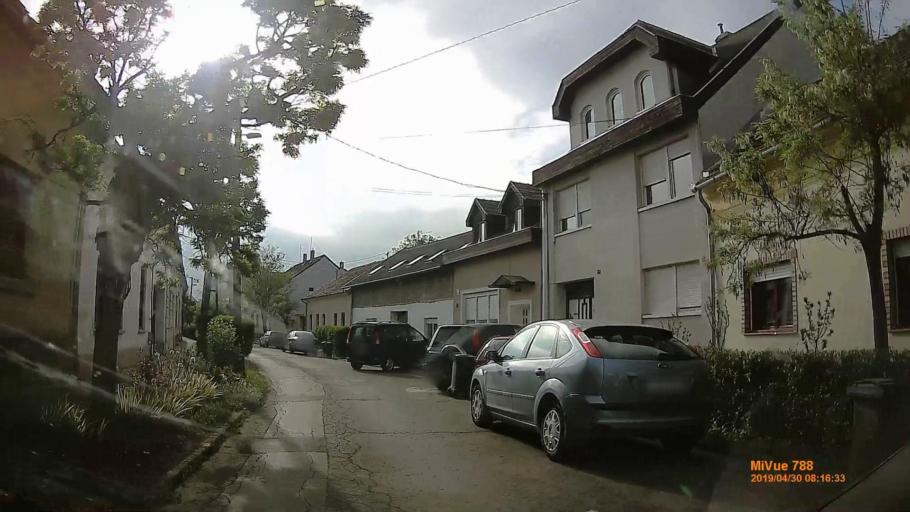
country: HU
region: Pest
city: Vac
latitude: 47.7725
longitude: 19.1369
